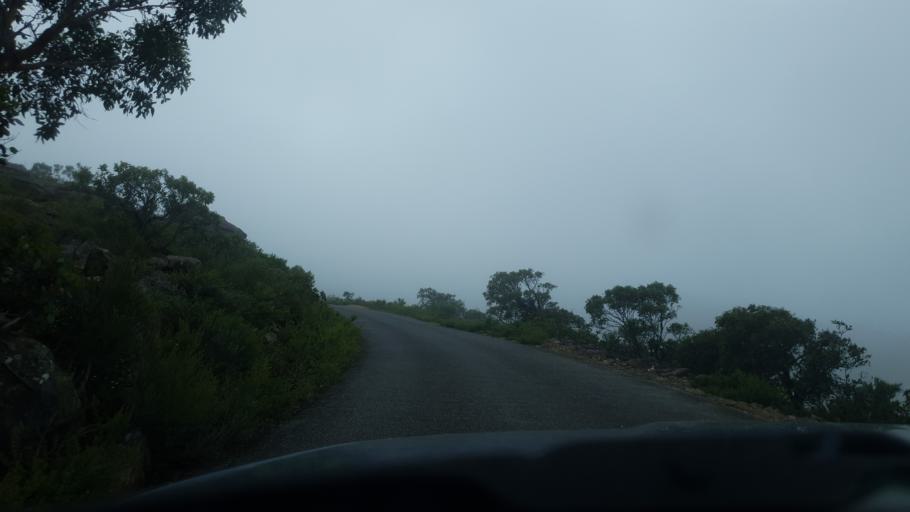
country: AU
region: Victoria
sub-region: Northern Grampians
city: Stawell
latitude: -37.2728
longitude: 142.5808
